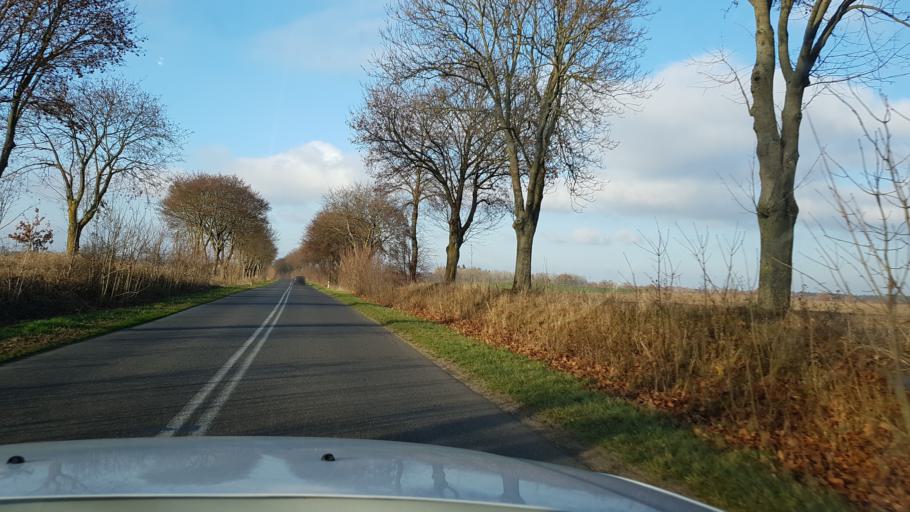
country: PL
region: West Pomeranian Voivodeship
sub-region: Powiat stargardzki
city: Chociwel
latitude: 53.4509
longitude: 15.3459
